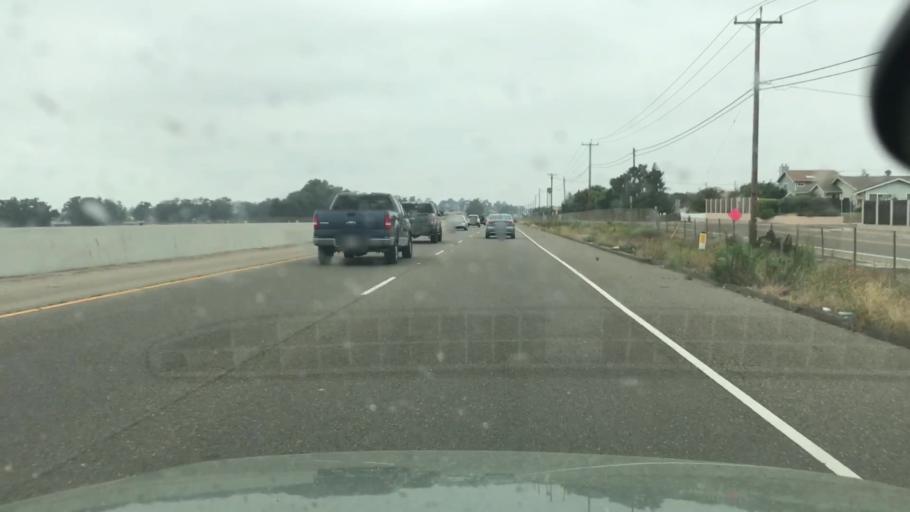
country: US
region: California
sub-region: Santa Barbara County
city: Orcutt
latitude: 34.8849
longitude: -120.4364
